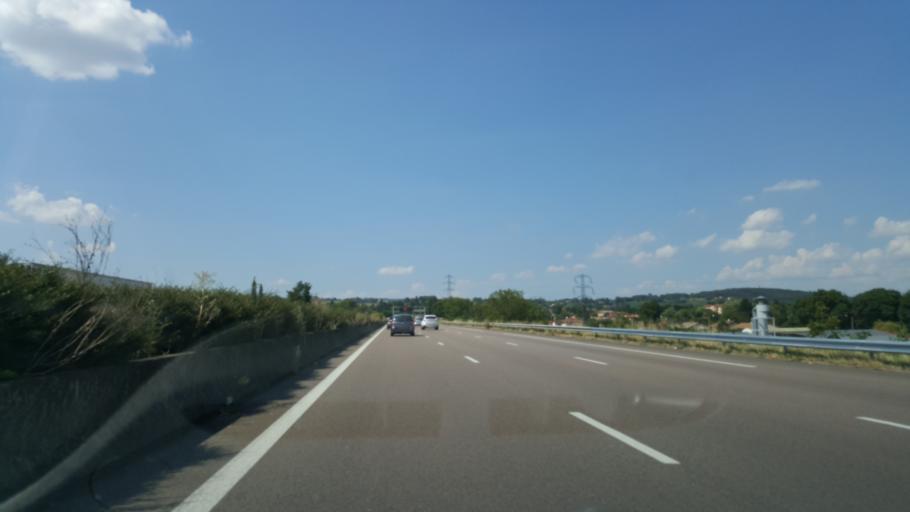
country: FR
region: Bourgogne
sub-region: Departement de Saone-et-Loire
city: Tournus
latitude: 46.5525
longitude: 4.9062
